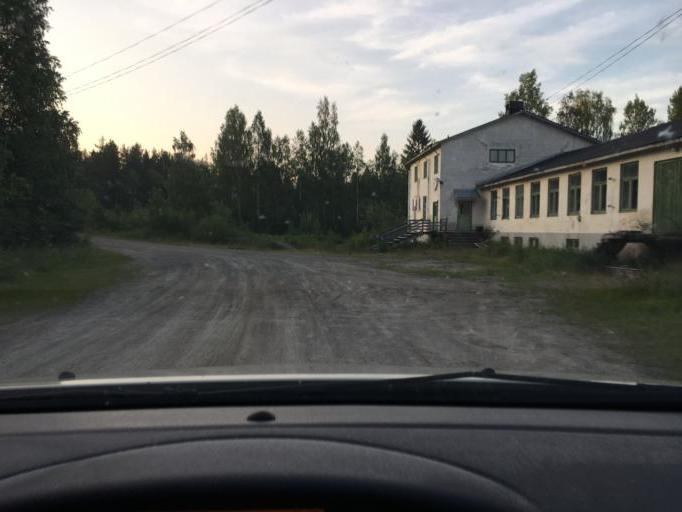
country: SE
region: Norrbotten
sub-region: Kalix Kommun
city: Toere
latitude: 66.0735
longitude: 22.7283
